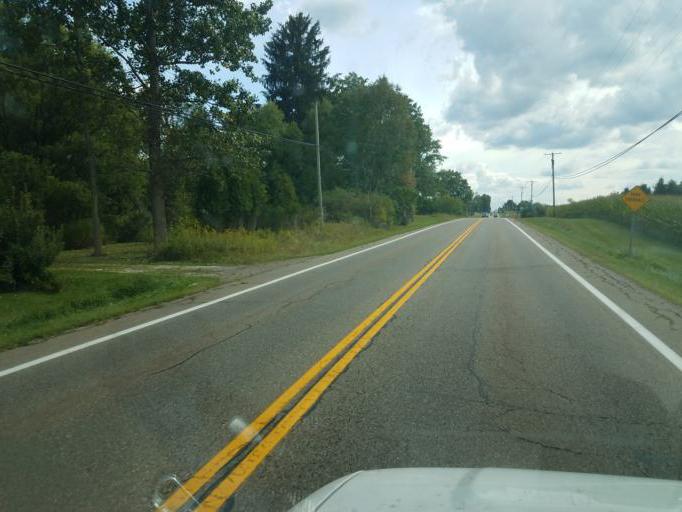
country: US
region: Ohio
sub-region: Portage County
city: Ravenna
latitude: 41.0518
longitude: -81.2477
